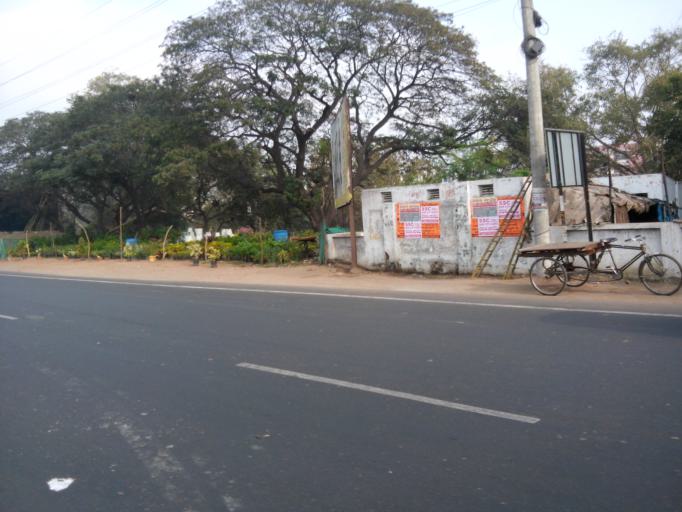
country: IN
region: Andhra Pradesh
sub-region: Krishna
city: Vijayawada
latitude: 16.5090
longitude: 80.6215
